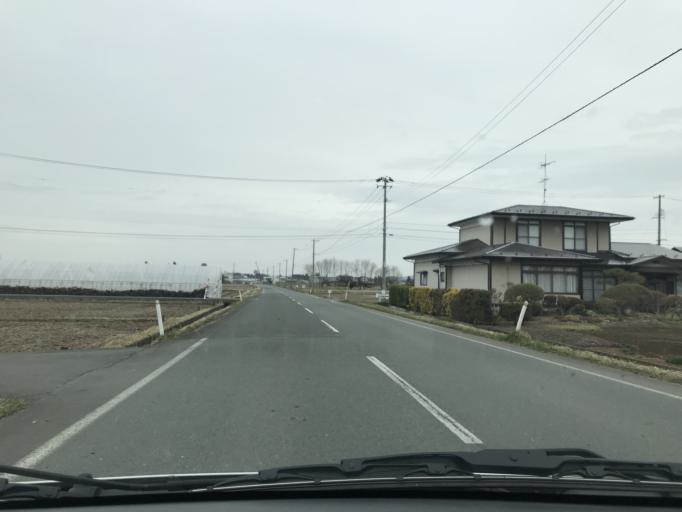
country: JP
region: Iwate
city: Mizusawa
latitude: 39.1733
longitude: 141.1137
